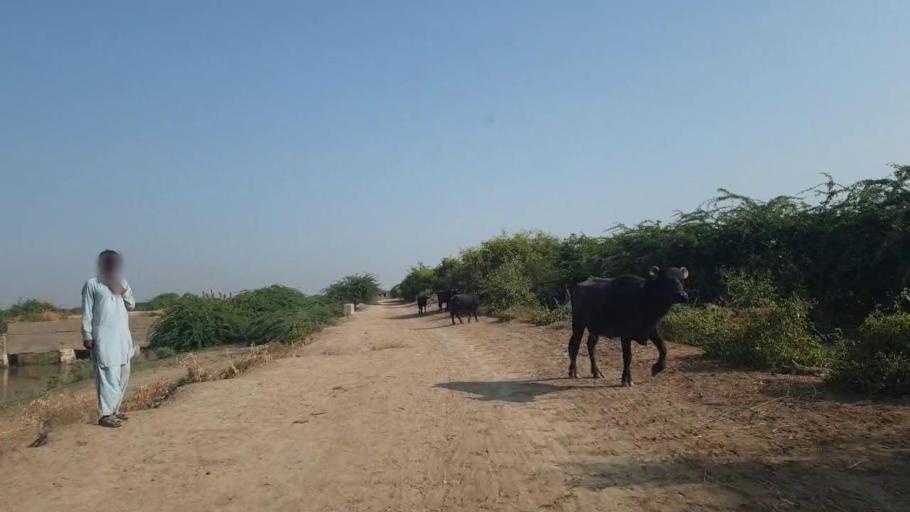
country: PK
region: Sindh
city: Badin
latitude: 24.4660
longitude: 68.7389
